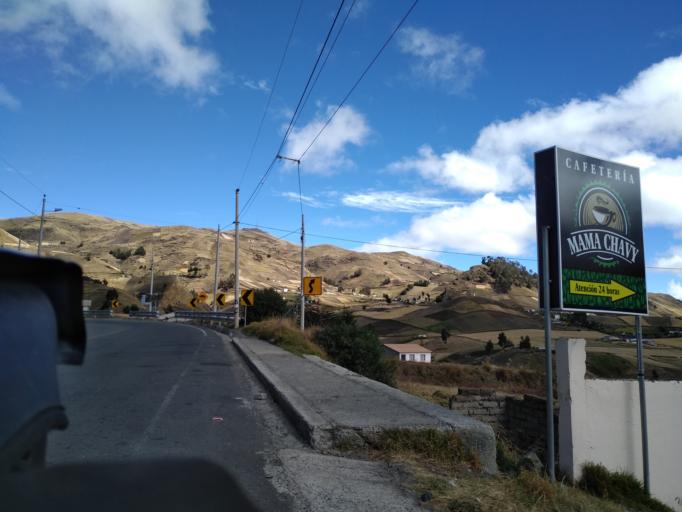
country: EC
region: Cotopaxi
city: Pujili
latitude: -0.9647
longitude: -78.9017
